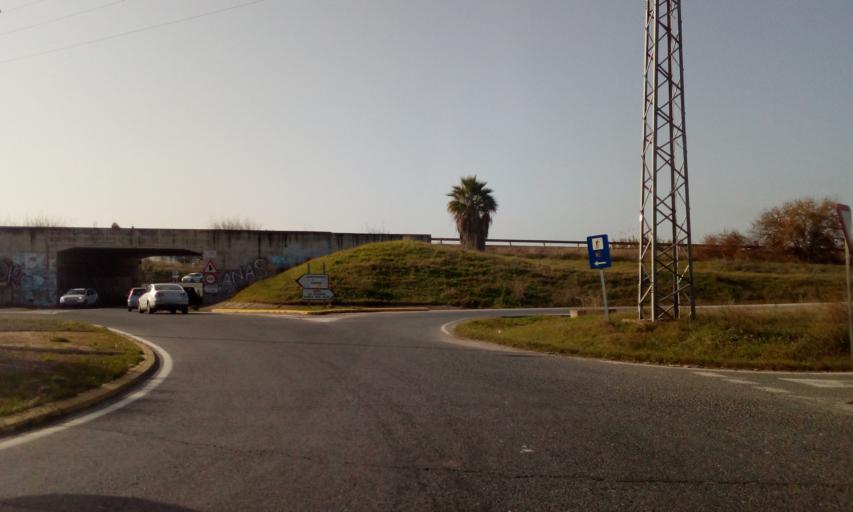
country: ES
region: Andalusia
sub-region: Provincia de Sevilla
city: Santiponce
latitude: 37.4306
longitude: -6.0345
